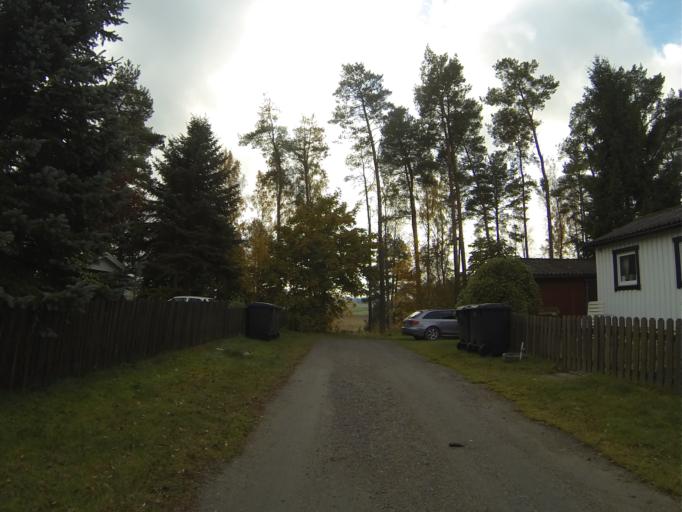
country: SE
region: Skane
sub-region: Sjobo Kommun
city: Blentarp
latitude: 55.6315
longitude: 13.6371
